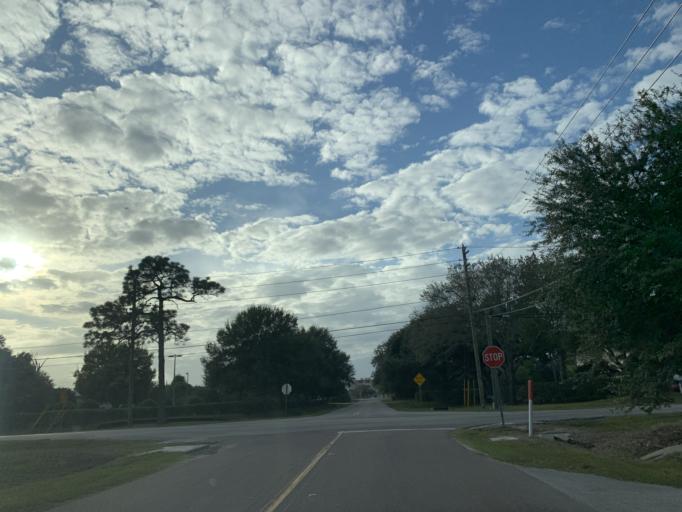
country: US
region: Florida
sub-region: Pinellas County
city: South Highpoint
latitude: 27.9029
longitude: -82.6962
